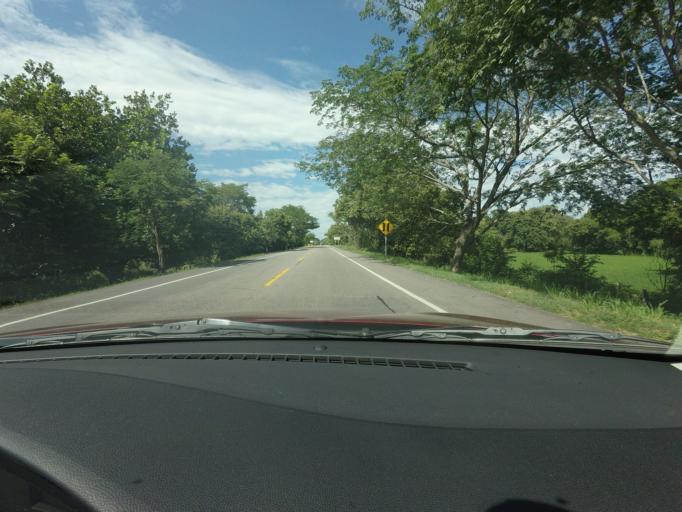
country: CO
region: Tolima
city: Natagaima
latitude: 3.7229
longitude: -75.0794
